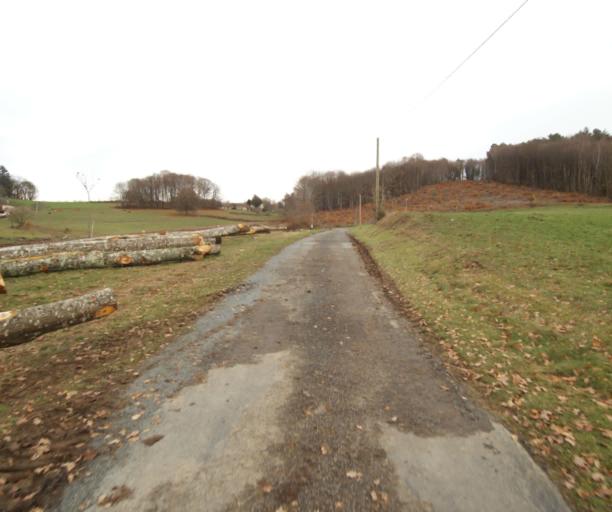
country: FR
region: Limousin
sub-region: Departement de la Correze
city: Chameyrat
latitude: 45.2533
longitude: 1.6733
